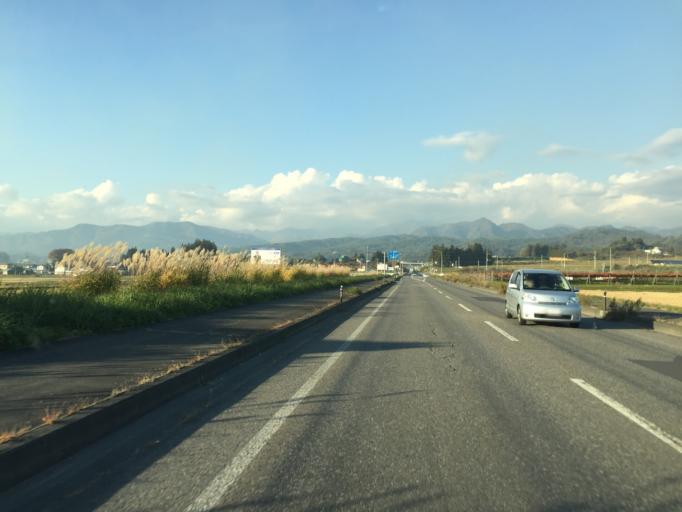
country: JP
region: Fukushima
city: Kitakata
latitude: 37.6803
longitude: 139.8885
